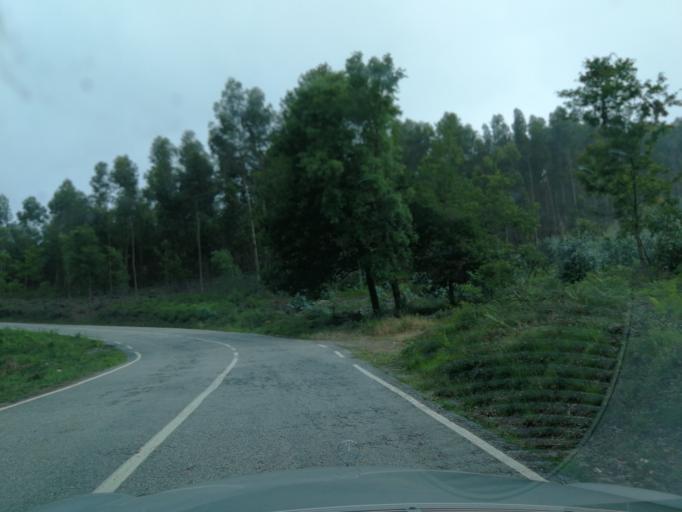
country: PT
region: Braga
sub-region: Braga
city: Braga
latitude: 41.5209
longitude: -8.3803
